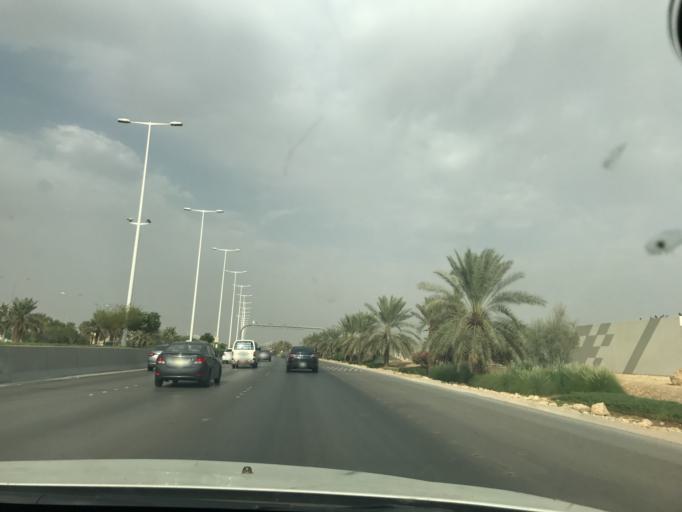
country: SA
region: Ar Riyad
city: Riyadh
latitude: 24.7230
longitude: 46.6982
